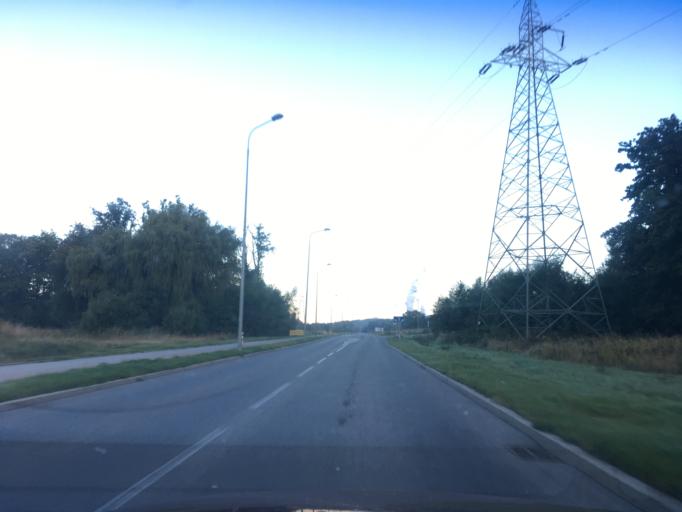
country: PL
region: Lower Silesian Voivodeship
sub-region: Powiat zgorzelecki
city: Bogatynia
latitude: 50.9147
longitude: 14.9608
